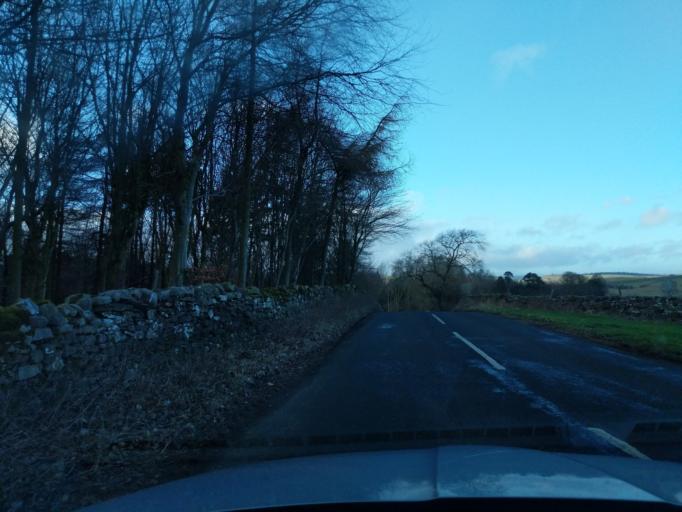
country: GB
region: England
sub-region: North Yorkshire
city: Leyburn
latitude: 54.3581
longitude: -1.8208
